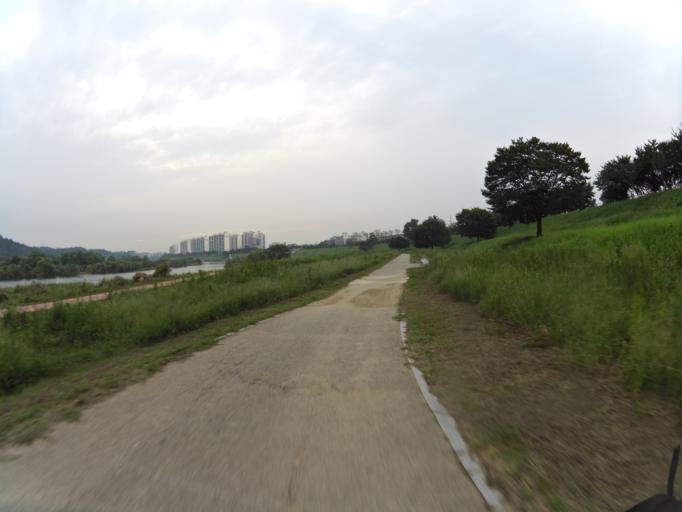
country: KR
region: Gyeongsangbuk-do
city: Gyeongsan-si
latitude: 35.8734
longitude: 128.6780
